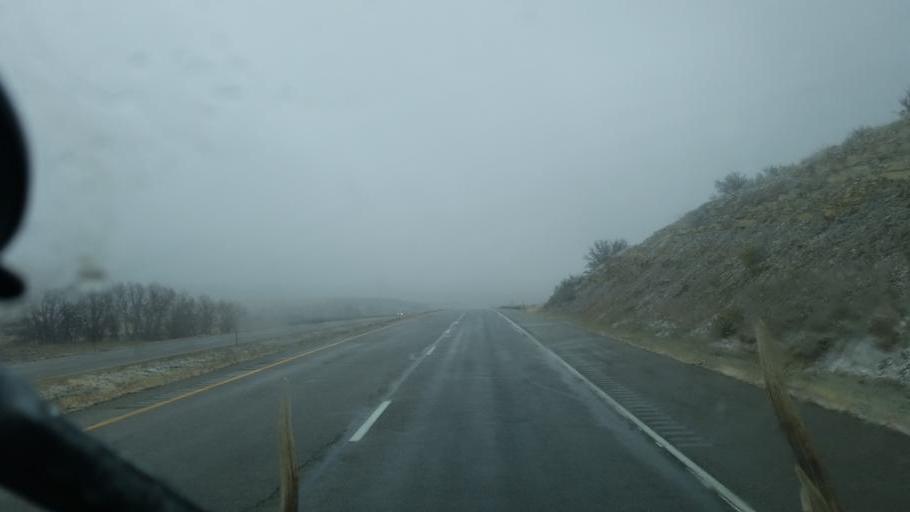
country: US
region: Colorado
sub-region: Pueblo County
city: Colorado City
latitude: 37.8992
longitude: -104.8288
